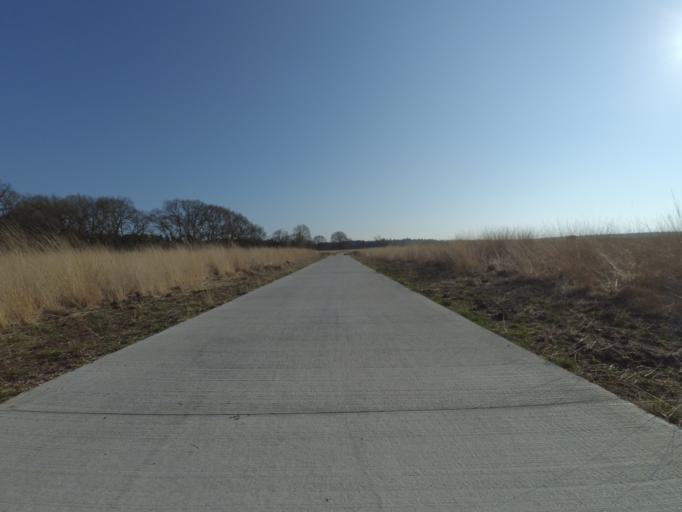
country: NL
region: Gelderland
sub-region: Gemeente Ede
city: Otterlo
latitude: 52.1008
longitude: 5.8653
